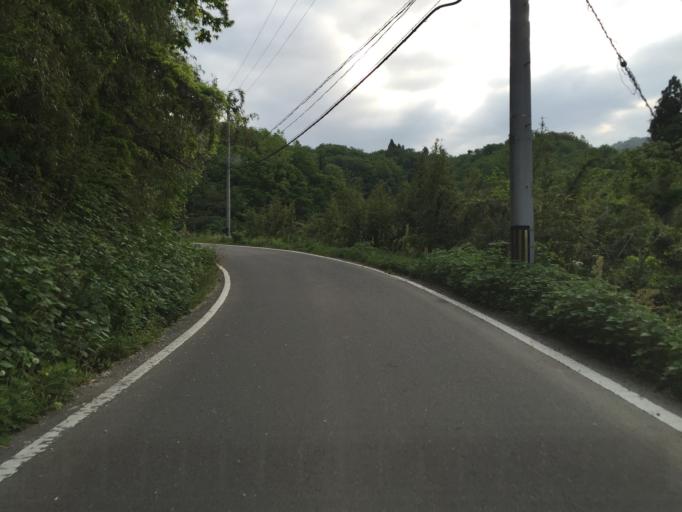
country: JP
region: Fukushima
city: Yanagawamachi-saiwaicho
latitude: 37.8978
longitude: 140.6742
